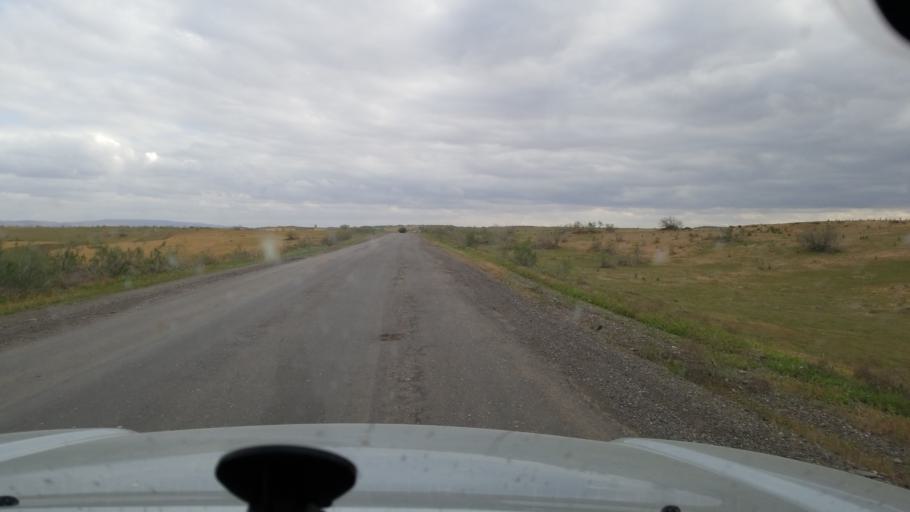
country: TM
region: Mary
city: Serhetabat
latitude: 35.9947
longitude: 62.6273
